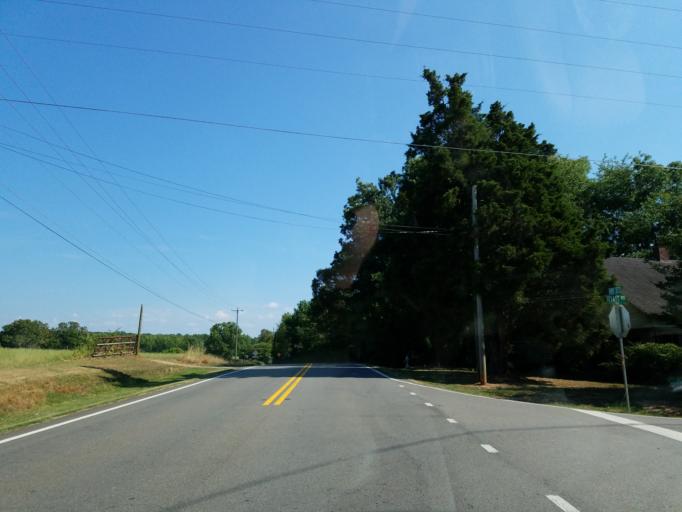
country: US
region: Georgia
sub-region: Fulton County
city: Milton
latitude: 34.2334
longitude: -84.2910
